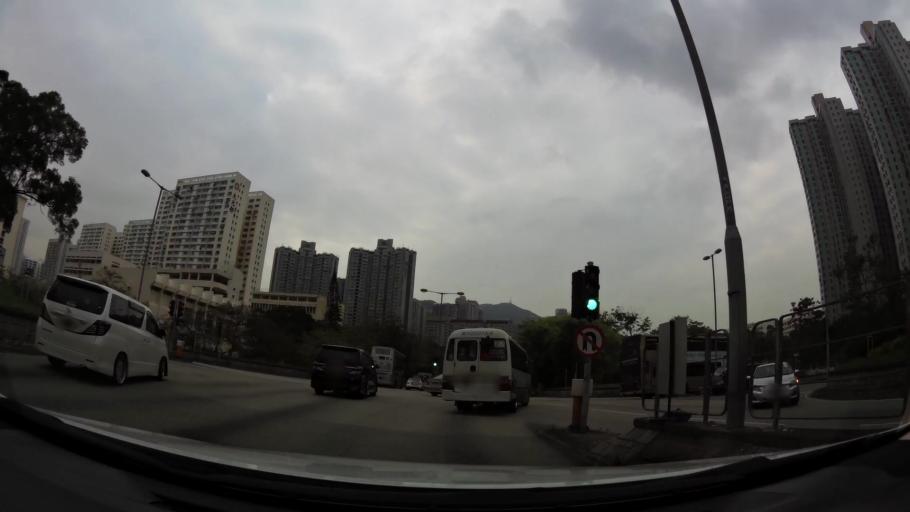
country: HK
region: Tai Po
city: Tai Po
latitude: 22.4541
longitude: 114.1722
